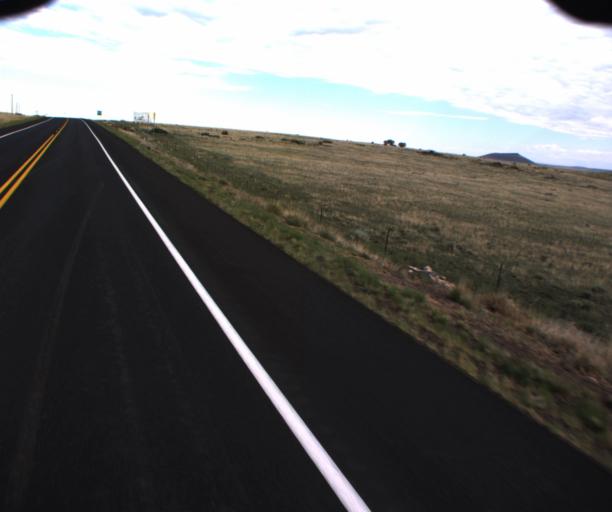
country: US
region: Arizona
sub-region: Apache County
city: Springerville
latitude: 34.1658
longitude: -109.3088
